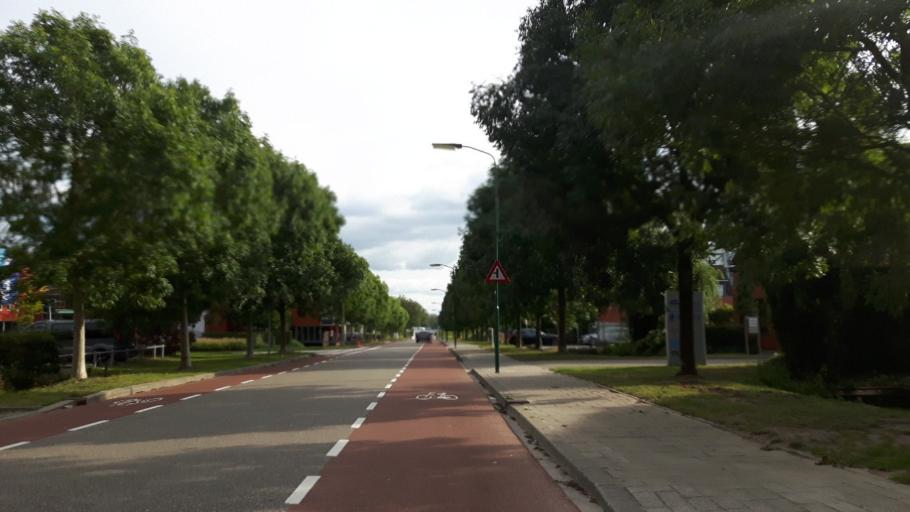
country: NL
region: Utrecht
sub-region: Gemeente Woerden
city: Woerden
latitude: 52.0785
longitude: 4.8982
